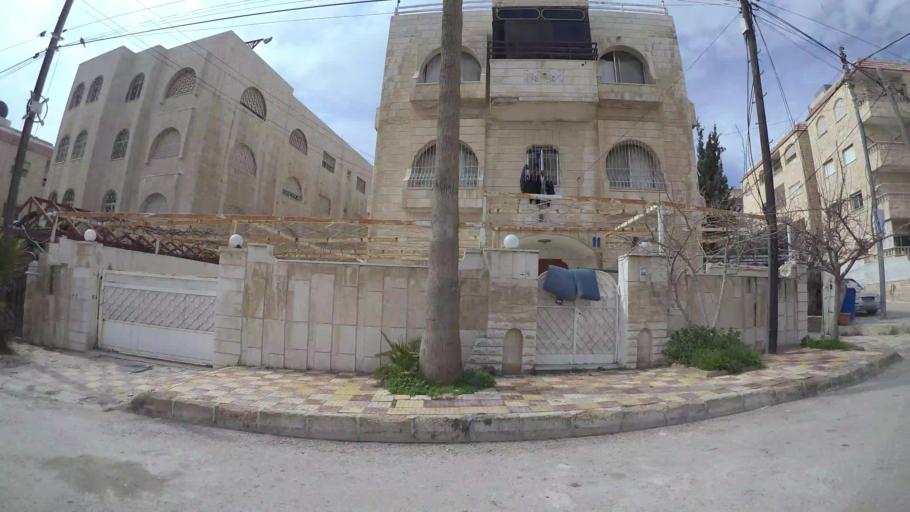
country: JO
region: Amman
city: Amman
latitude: 31.9922
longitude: 35.9406
